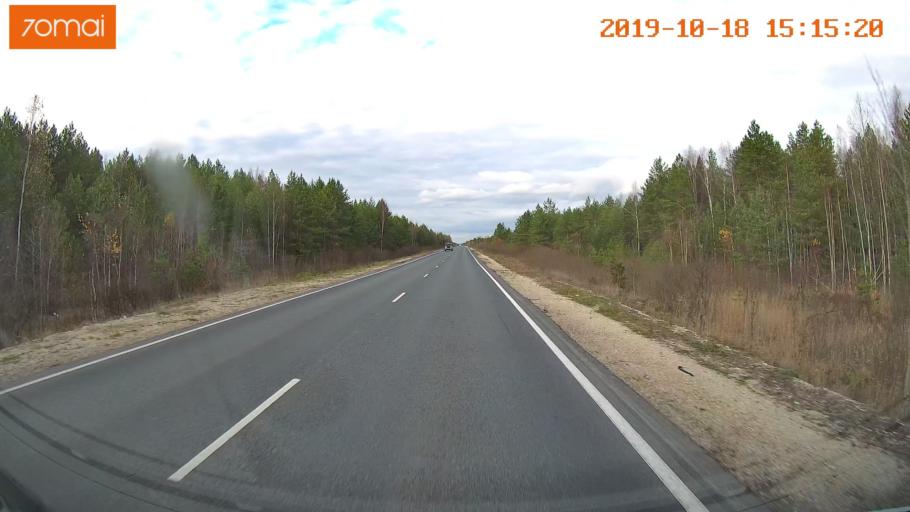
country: RU
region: Vladimir
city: Gus'-Khrustal'nyy
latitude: 55.6172
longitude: 40.7222
